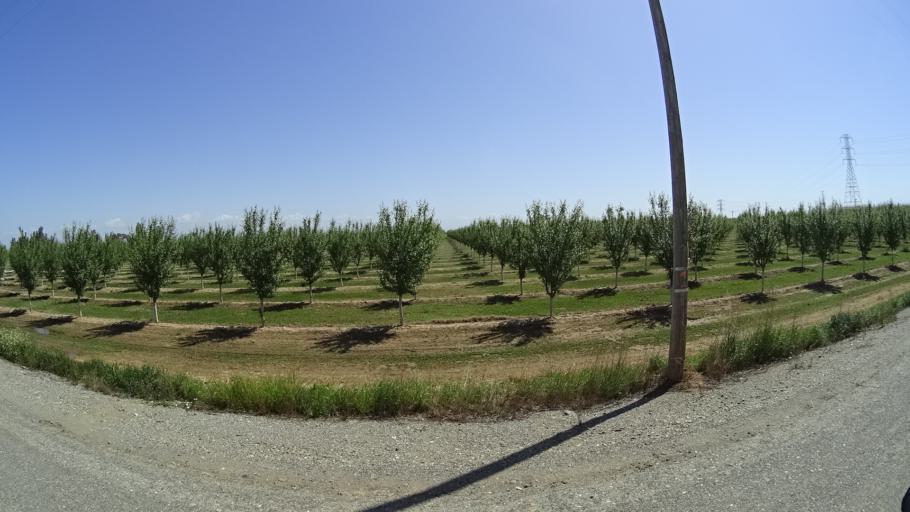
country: US
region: California
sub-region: Glenn County
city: Orland
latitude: 39.7881
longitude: -122.1503
